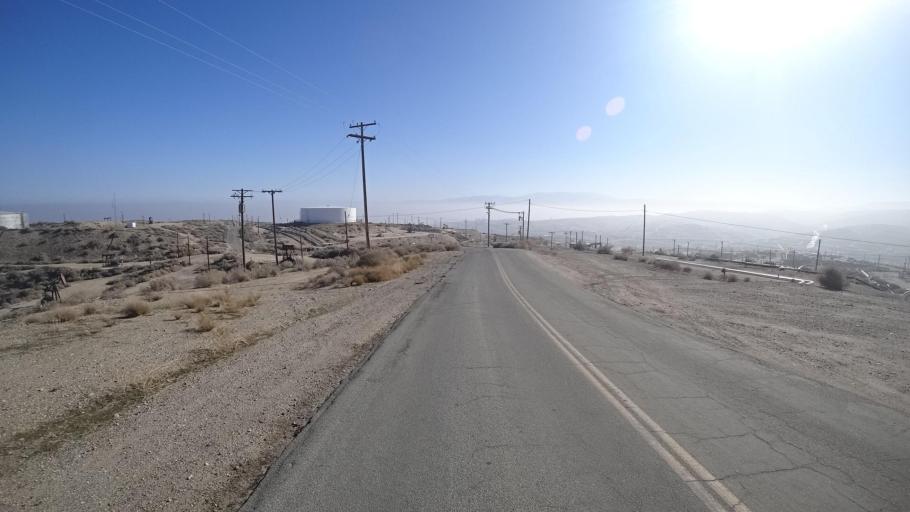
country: US
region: California
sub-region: Kern County
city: Taft Heights
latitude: 35.1144
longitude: -119.4669
